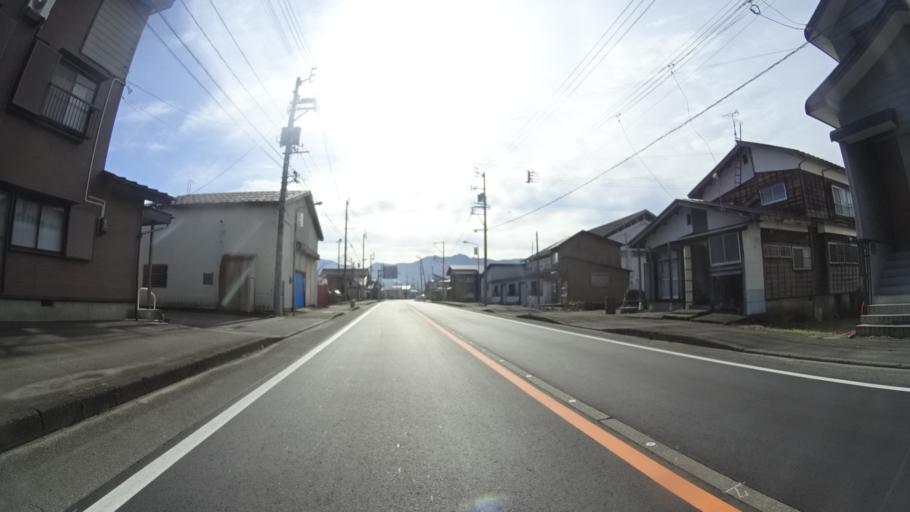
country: JP
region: Niigata
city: Muikamachi
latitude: 37.0985
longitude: 138.9190
